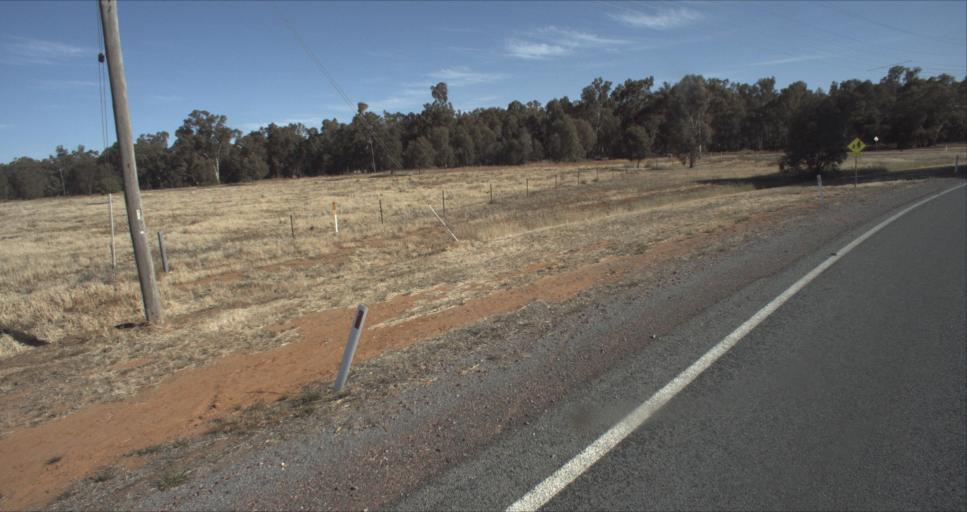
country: AU
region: New South Wales
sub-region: Leeton
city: Leeton
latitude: -34.6251
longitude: 146.3945
